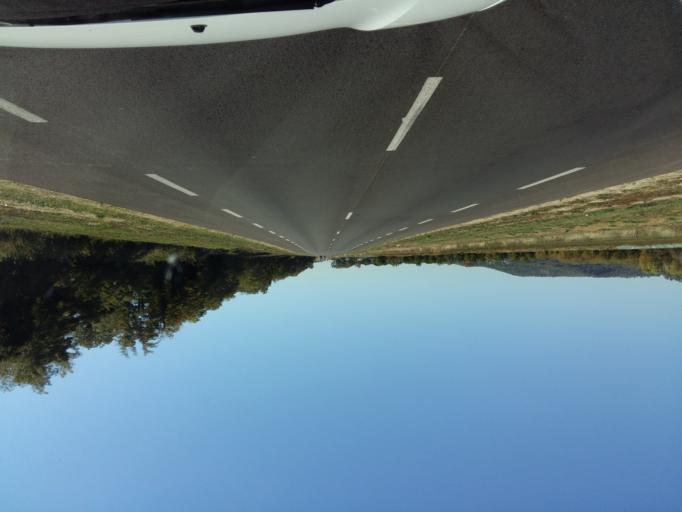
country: FR
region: Provence-Alpes-Cote d'Azur
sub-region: Departement du Vaucluse
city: Cadenet
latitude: 43.7178
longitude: 5.3991
